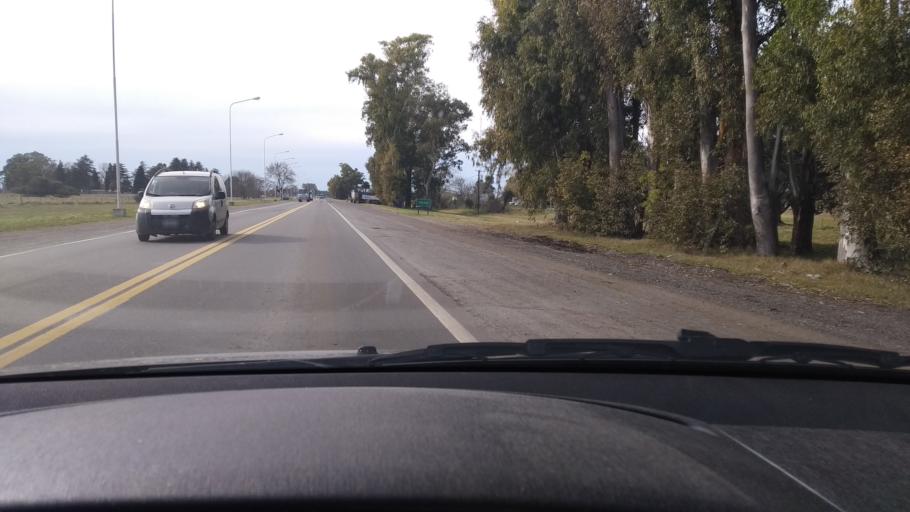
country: AR
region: Buenos Aires
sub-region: Partido de Azul
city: Azul
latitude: -36.7840
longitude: -59.8309
